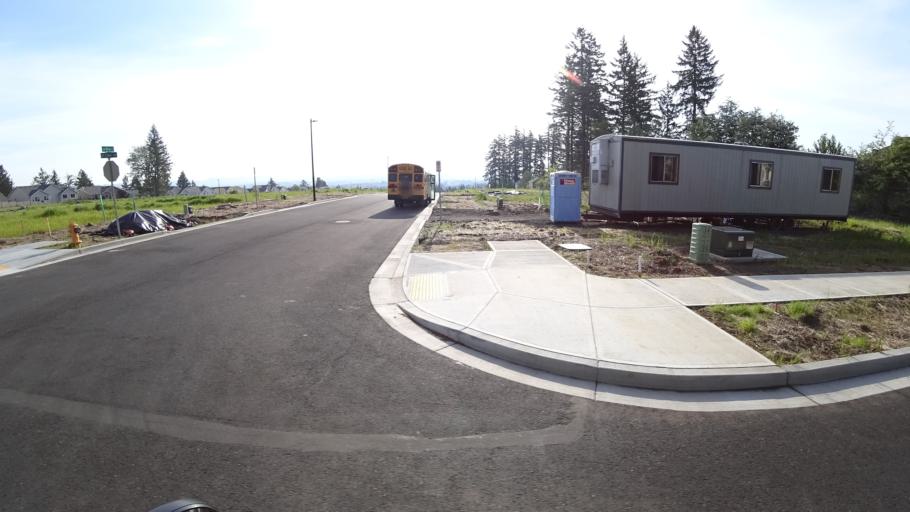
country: US
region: Oregon
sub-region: Washington County
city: King City
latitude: 45.4349
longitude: -122.8430
